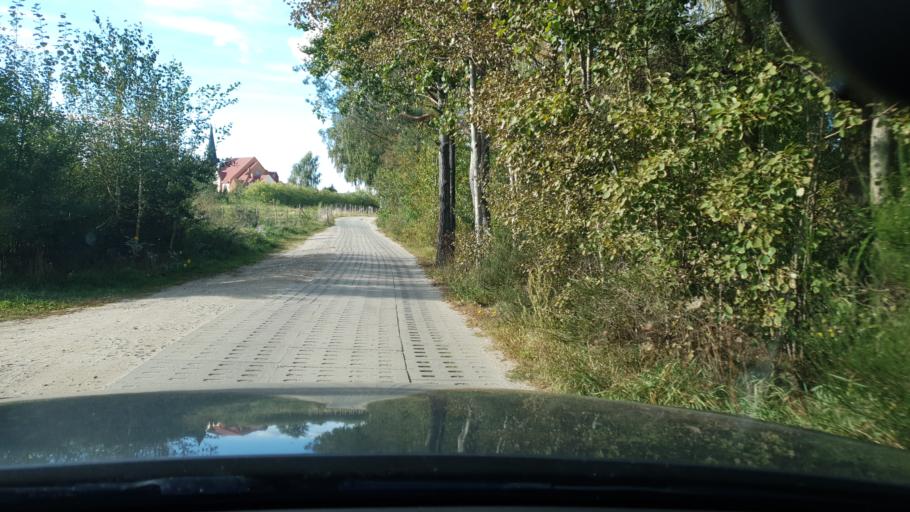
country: PL
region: Pomeranian Voivodeship
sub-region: Powiat kartuski
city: Chwaszczyno
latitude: 54.4840
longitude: 18.4234
